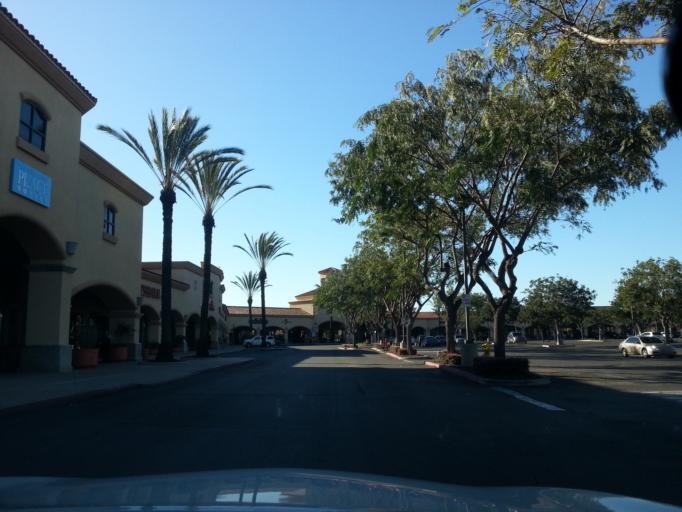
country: US
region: California
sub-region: Ventura County
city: Camarillo
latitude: 34.2150
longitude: -119.0576
